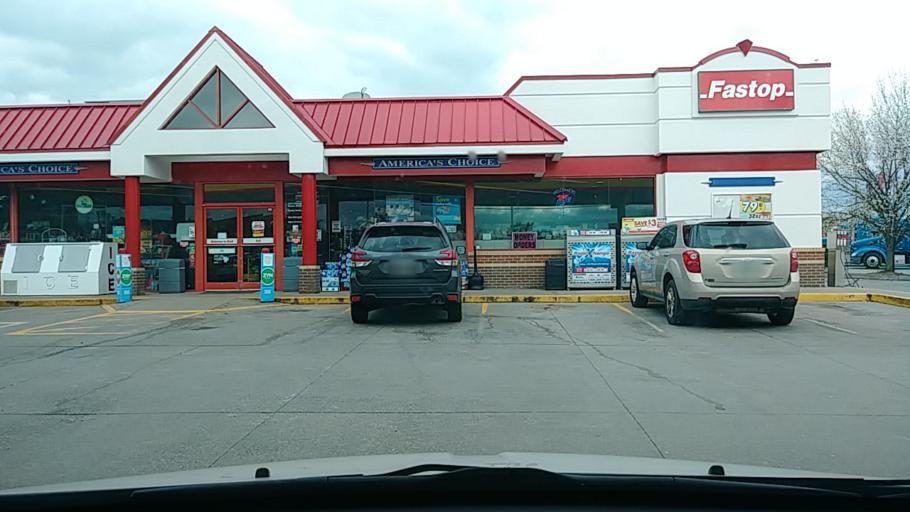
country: US
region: Tennessee
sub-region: Sevier County
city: Sevierville
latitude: 35.9866
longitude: -83.6071
